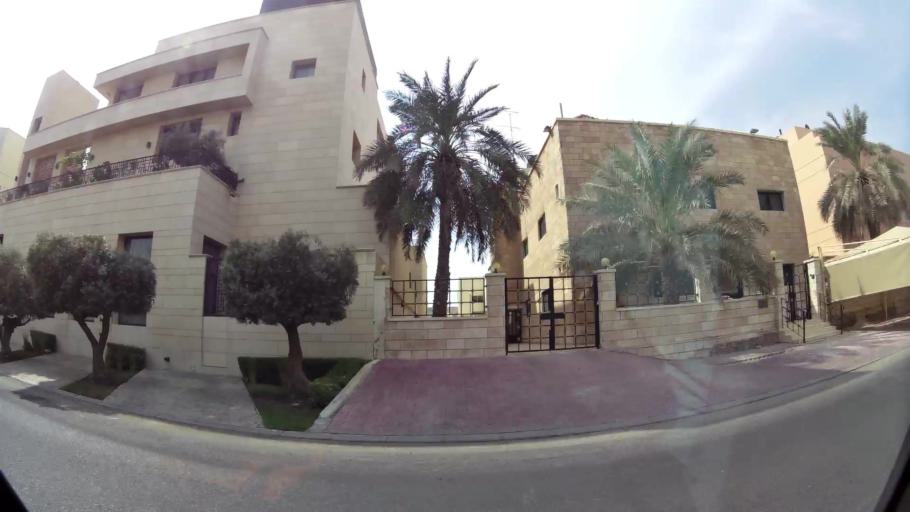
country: KW
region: Al Asimah
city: Ad Dasmah
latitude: 29.3546
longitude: 47.9886
